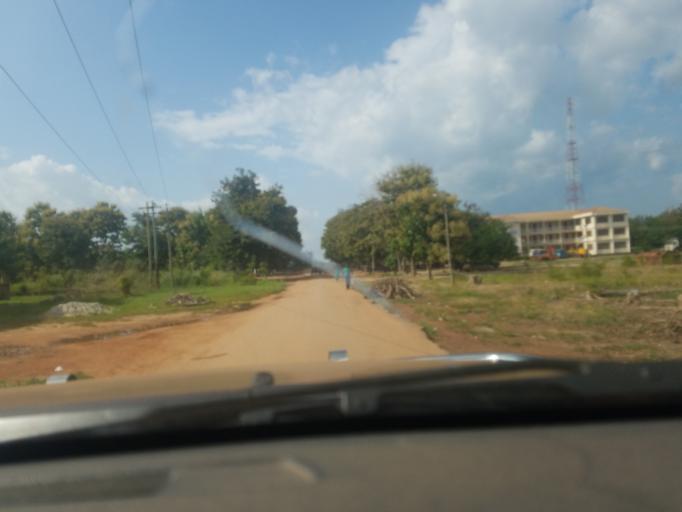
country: GH
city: Duayaw Nkwanta
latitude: 6.9791
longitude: -2.3829
